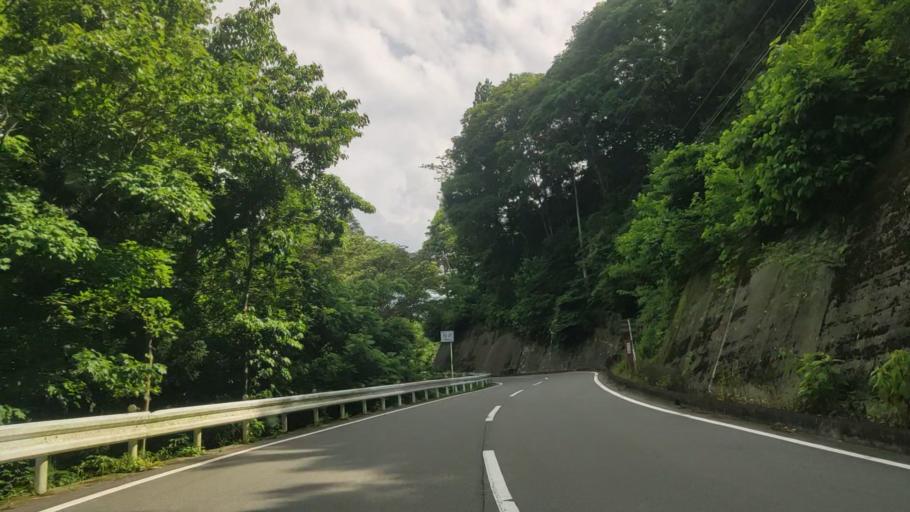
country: JP
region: Gunma
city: Tomioka
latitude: 36.1618
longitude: 138.7295
